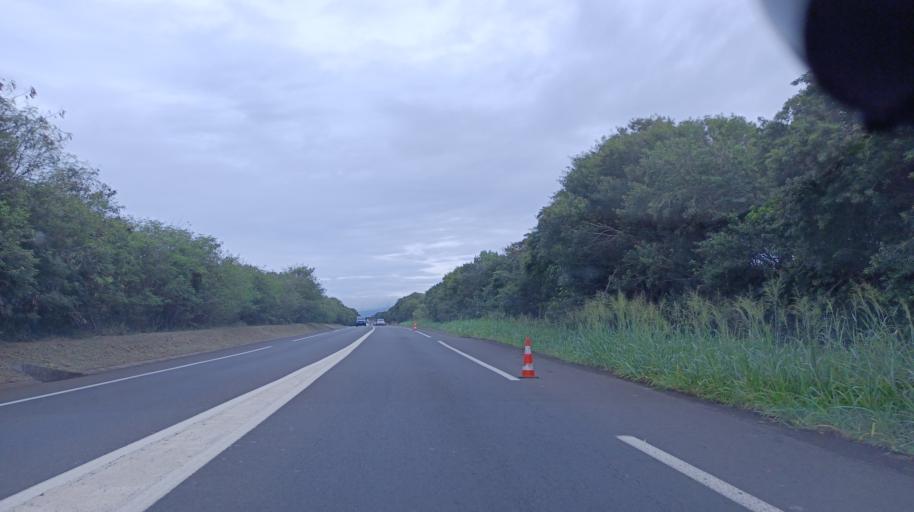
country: RE
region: Reunion
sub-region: Reunion
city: Saint-Pierre
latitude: -21.3438
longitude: 55.4973
